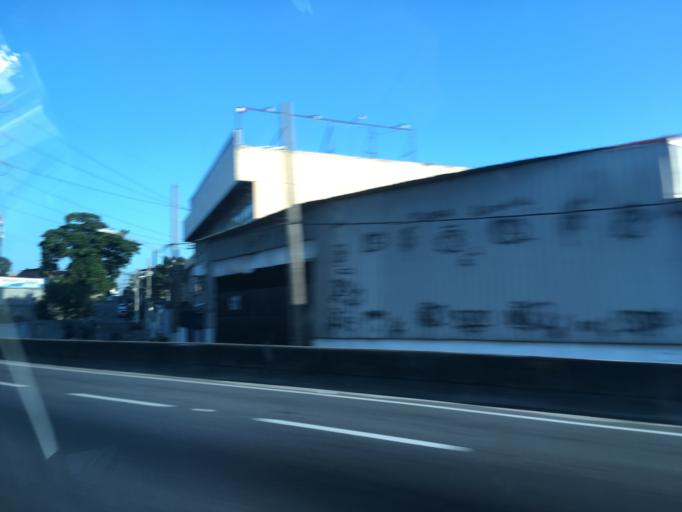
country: BR
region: Rio de Janeiro
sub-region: Sao Joao De Meriti
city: Sao Joao de Meriti
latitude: -22.7907
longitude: -43.3706
